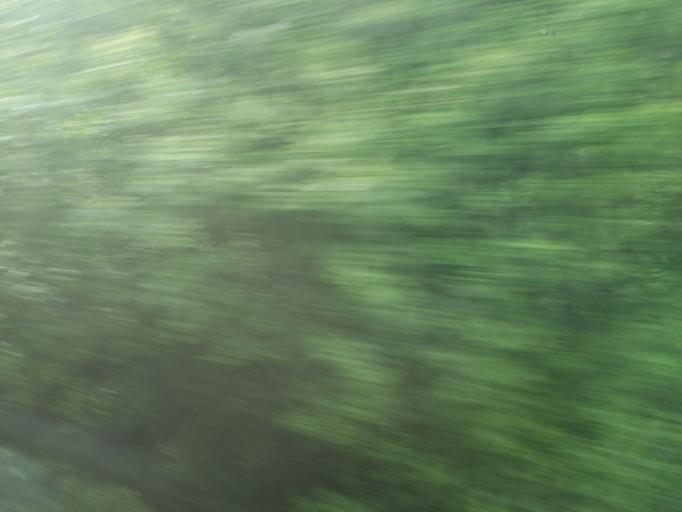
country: GB
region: England
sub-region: Devon
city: Winkleigh
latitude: 50.9824
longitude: -3.9693
